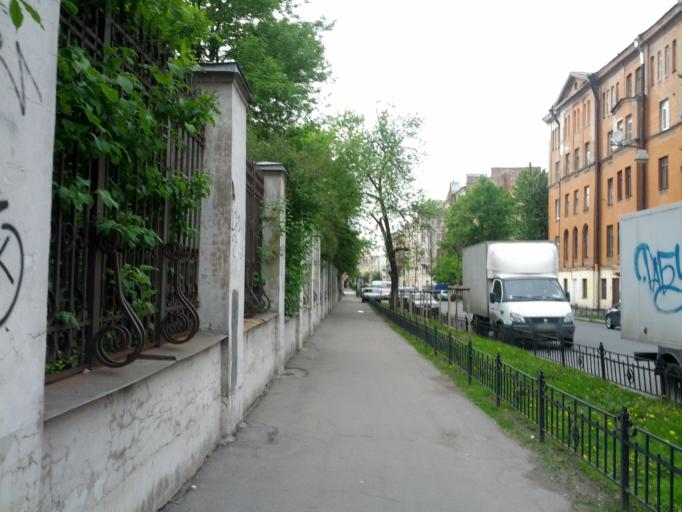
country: RU
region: St.-Petersburg
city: Centralniy
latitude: 59.9203
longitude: 30.3468
